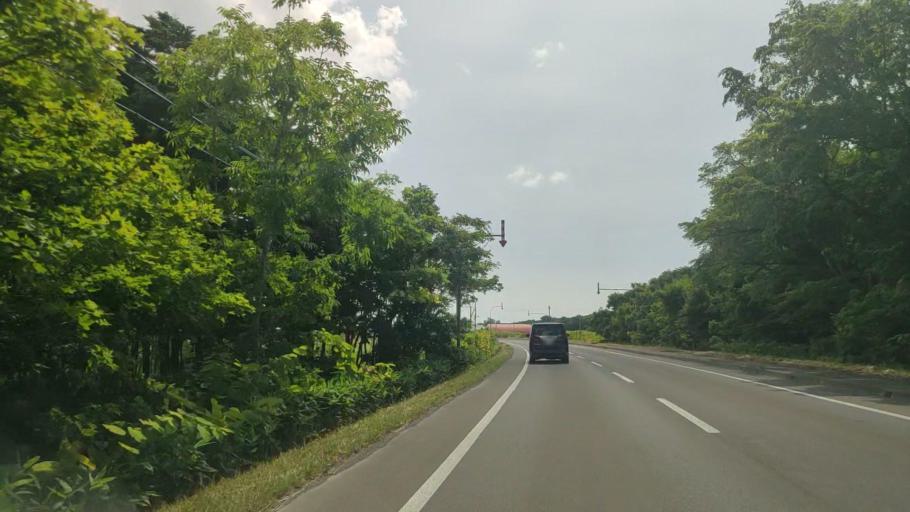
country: JP
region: Hokkaido
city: Makubetsu
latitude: 44.9053
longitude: 141.7385
